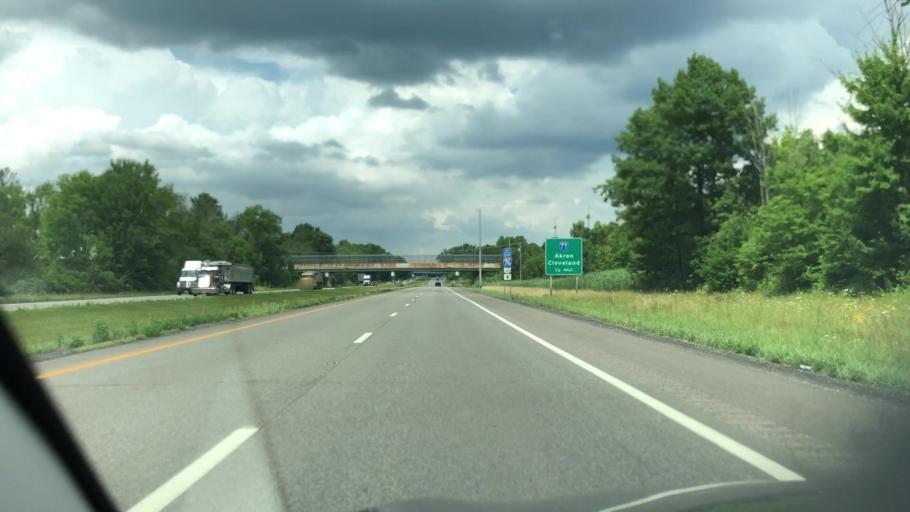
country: US
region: Ohio
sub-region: Summit County
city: Montrose-Ghent
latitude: 41.1092
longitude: -81.6553
